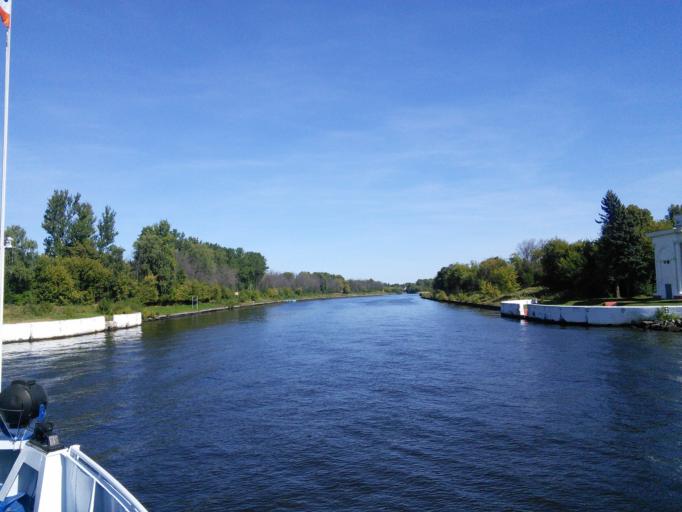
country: RU
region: Moskovskaya
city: Dolgoprudnyy
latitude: 55.9496
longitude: 37.4803
